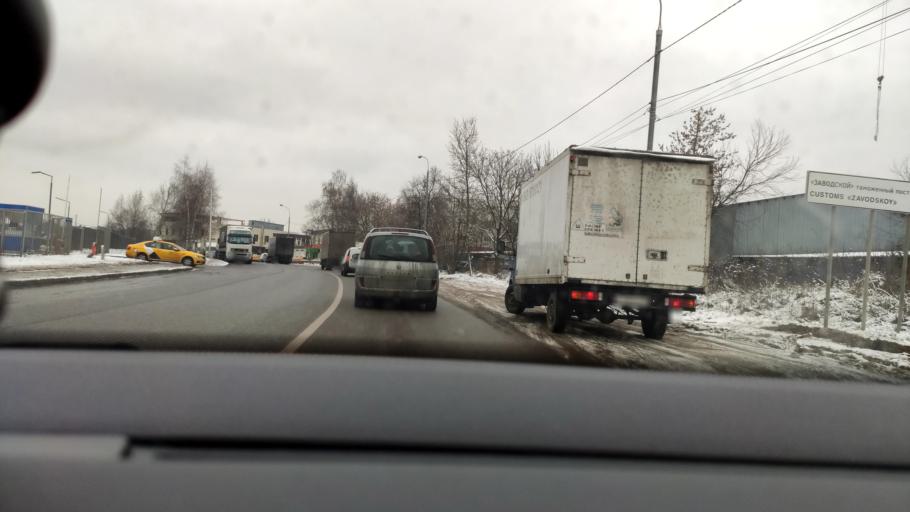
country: RU
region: Moscow
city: Khimki
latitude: 55.9170
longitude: 37.4219
